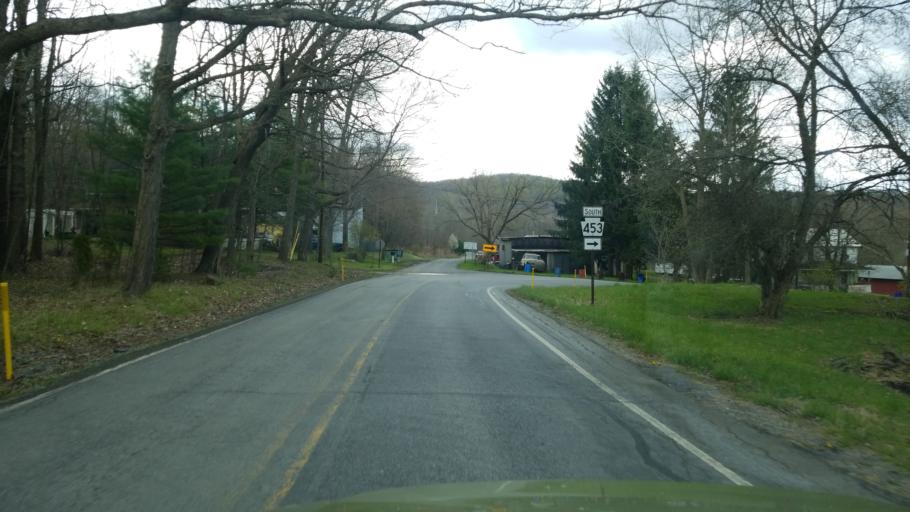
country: US
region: Pennsylvania
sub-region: Clearfield County
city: Curwensville
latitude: 40.8904
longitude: -78.4604
